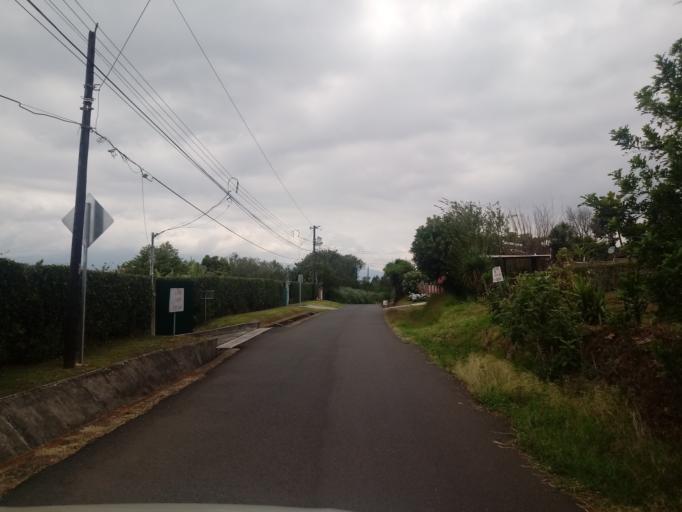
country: CR
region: Heredia
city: Angeles
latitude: 10.0337
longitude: -84.0416
